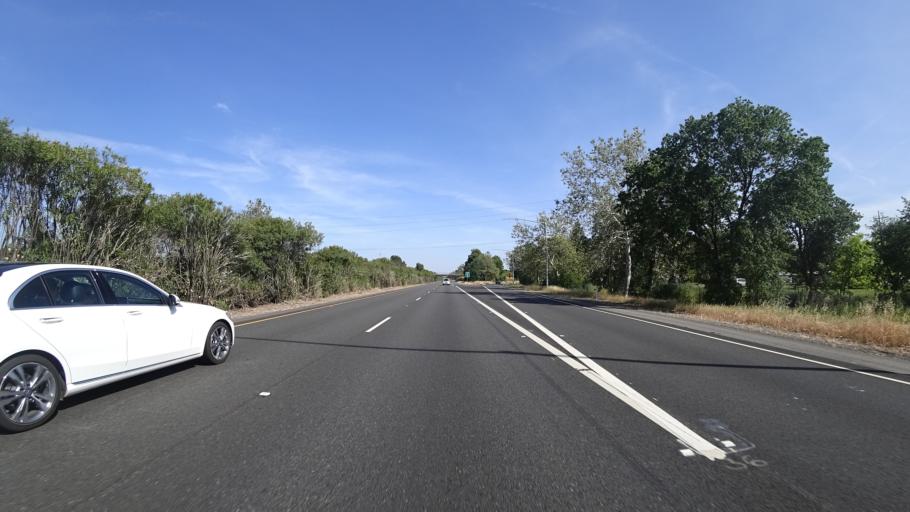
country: US
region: California
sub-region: Butte County
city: Chico
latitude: 39.7766
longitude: -121.8762
